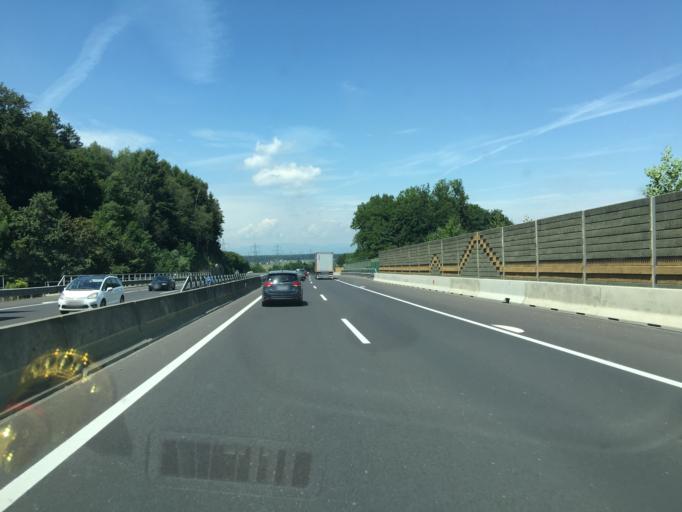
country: AT
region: Styria
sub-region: Politischer Bezirk Leibnitz
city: Weitendorf
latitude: 46.8763
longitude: 15.4812
